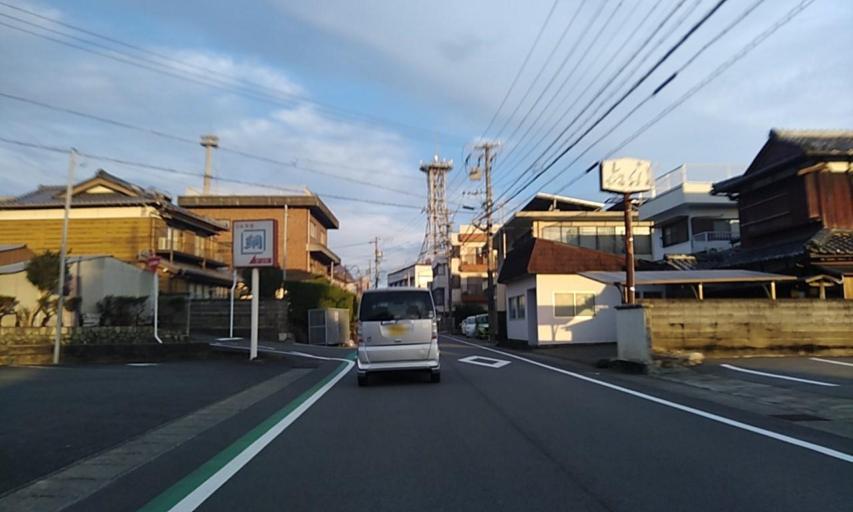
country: JP
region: Mie
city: Toba
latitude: 34.3297
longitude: 136.8277
